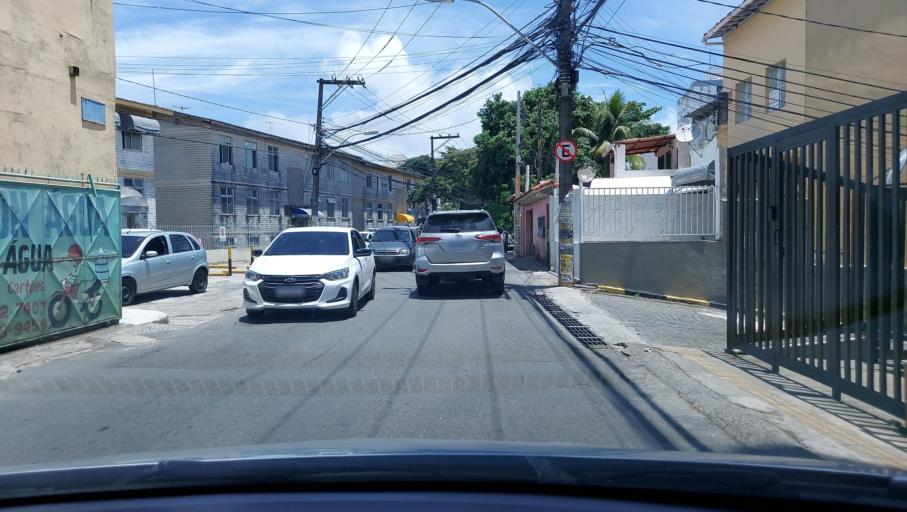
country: BR
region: Bahia
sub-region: Salvador
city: Salvador
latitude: -12.9862
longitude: -38.4753
